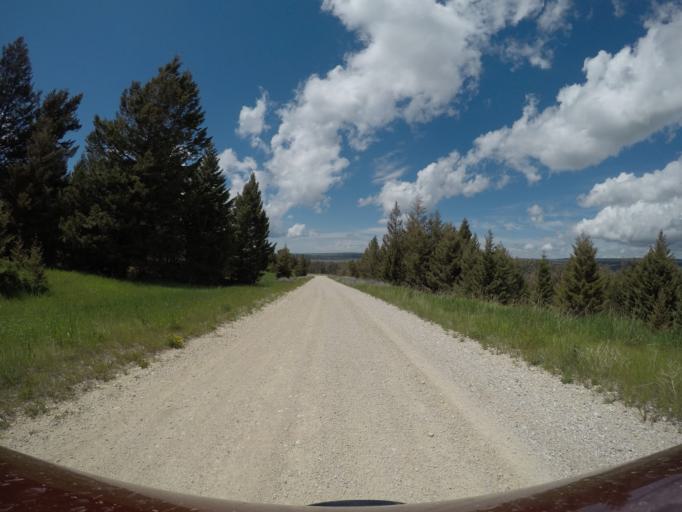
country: US
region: Wyoming
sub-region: Big Horn County
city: Lovell
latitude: 45.1951
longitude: -108.4837
